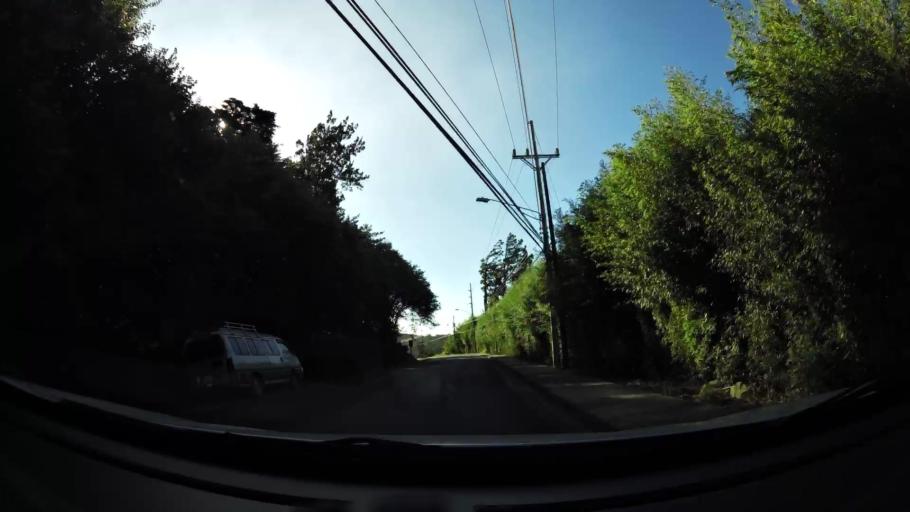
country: CR
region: Guanacaste
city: Juntas
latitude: 10.3123
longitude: -84.8157
